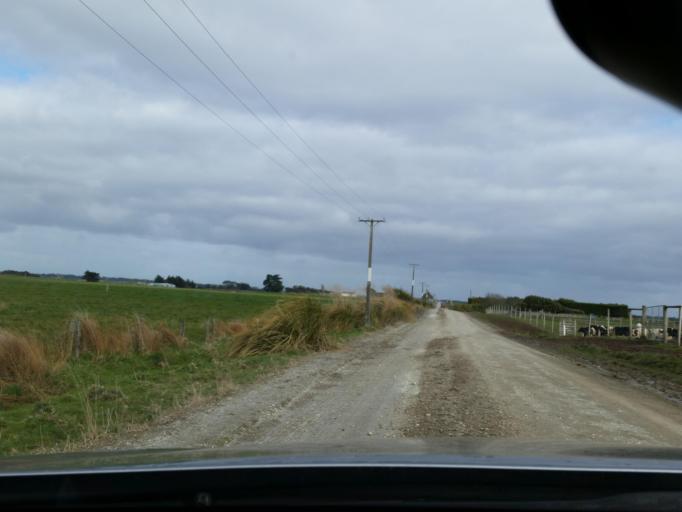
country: NZ
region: Southland
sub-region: Invercargill City
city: Invercargill
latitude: -46.4429
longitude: 168.5062
